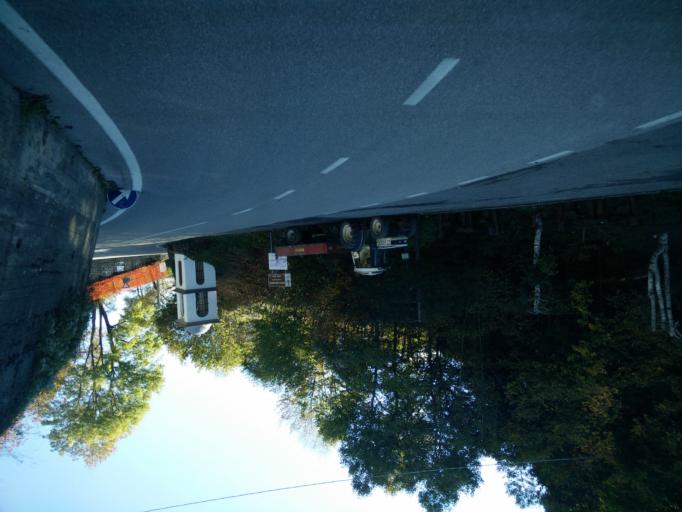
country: IT
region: Lombardy
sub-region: Provincia di Brescia
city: Capovalle
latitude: 45.7491
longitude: 10.5395
